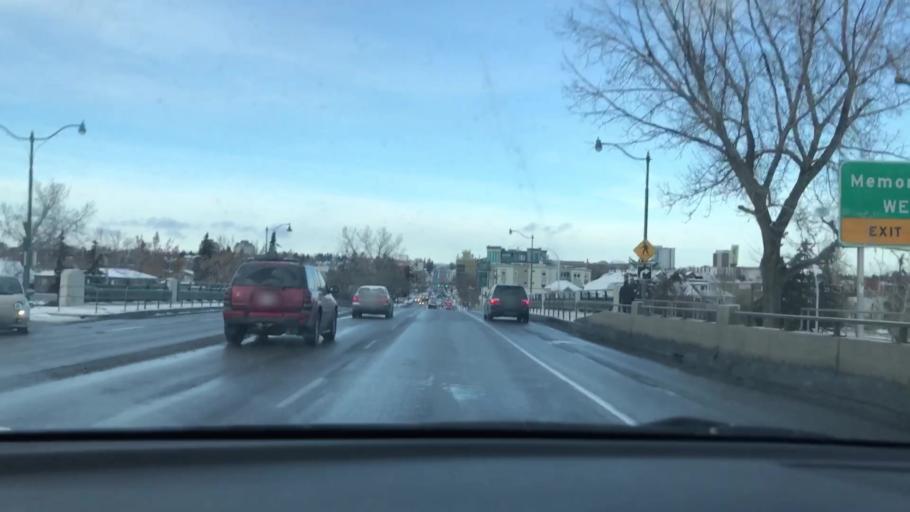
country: CA
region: Alberta
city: Calgary
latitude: 51.0488
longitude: -114.0947
